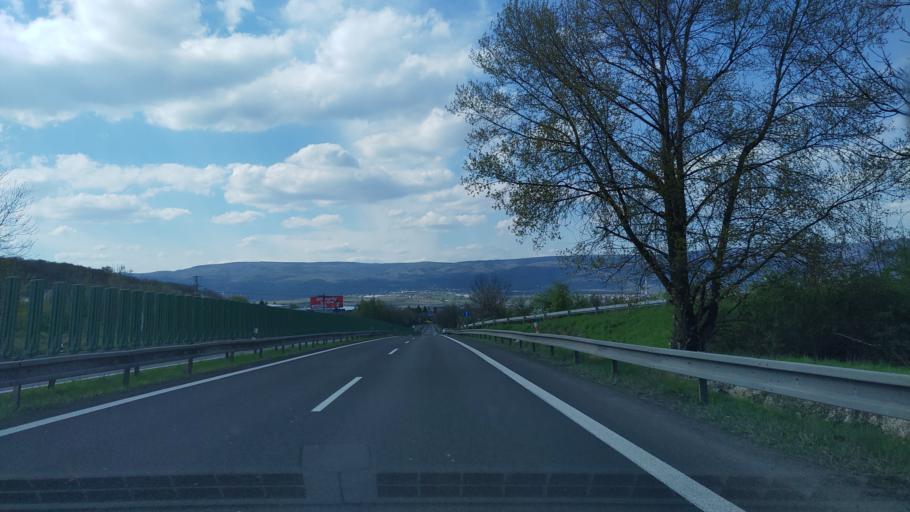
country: CZ
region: Ustecky
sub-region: Okres Teplice
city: Teplice
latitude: 50.6194
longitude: 13.8330
